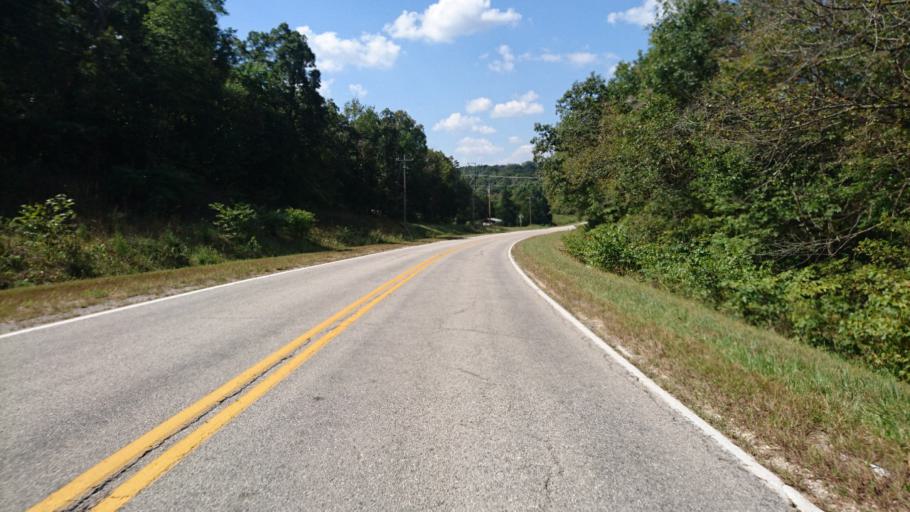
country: US
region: Missouri
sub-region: Pulaski County
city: Richland
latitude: 37.7525
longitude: -92.4900
